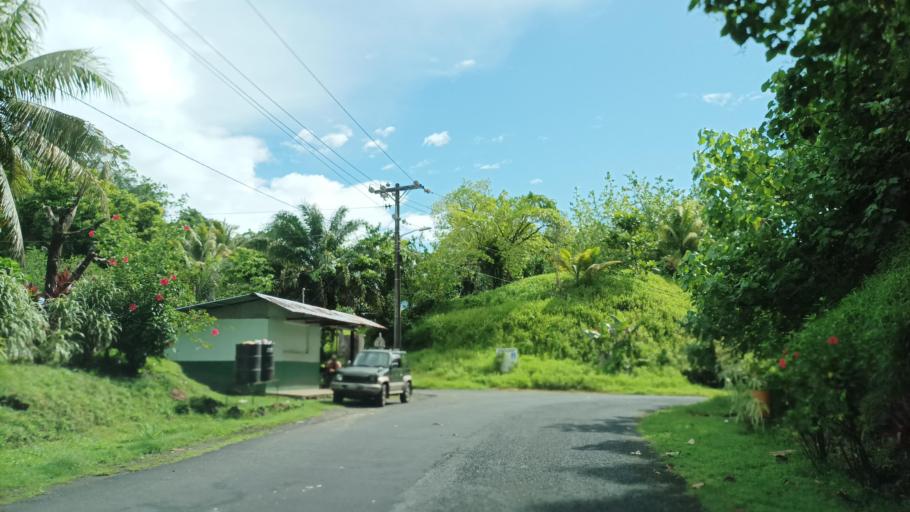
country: FM
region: Pohnpei
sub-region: Madolenihm Municipality
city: Madolenihm Municipality Government
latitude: 6.9210
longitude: 158.3097
